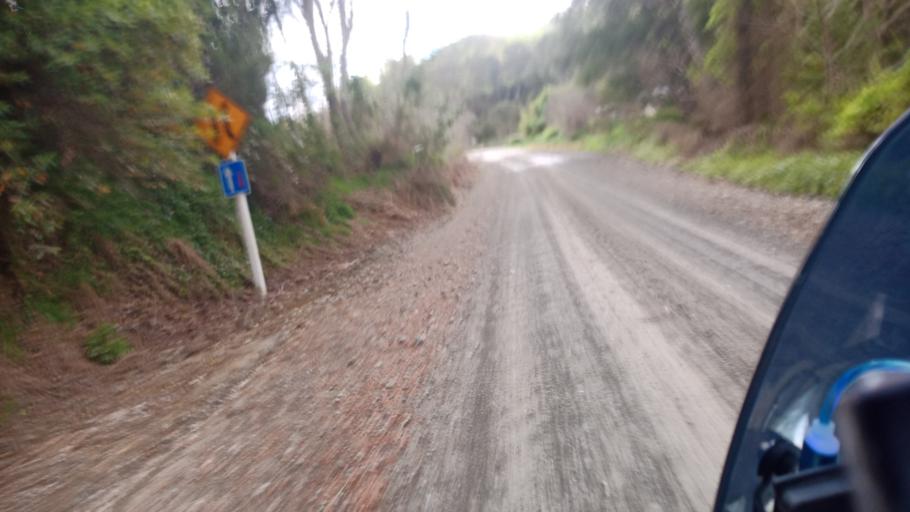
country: NZ
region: Gisborne
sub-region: Gisborne District
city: Gisborne
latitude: -38.2047
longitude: 178.2349
